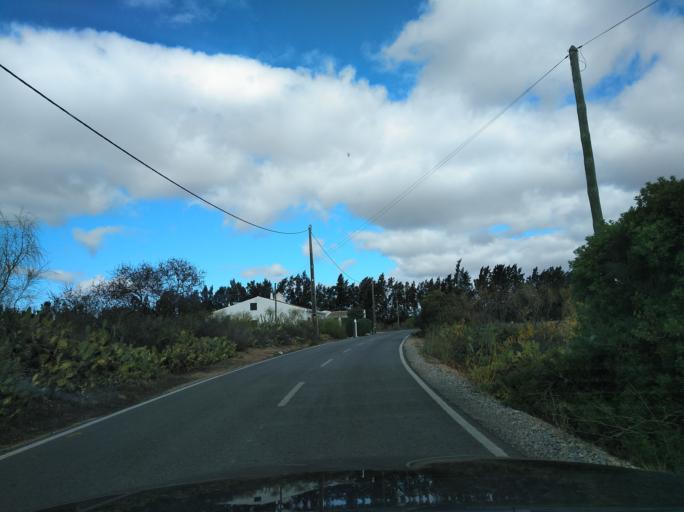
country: PT
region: Faro
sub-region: Vila Real de Santo Antonio
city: Monte Gordo
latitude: 37.1845
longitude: -7.4949
